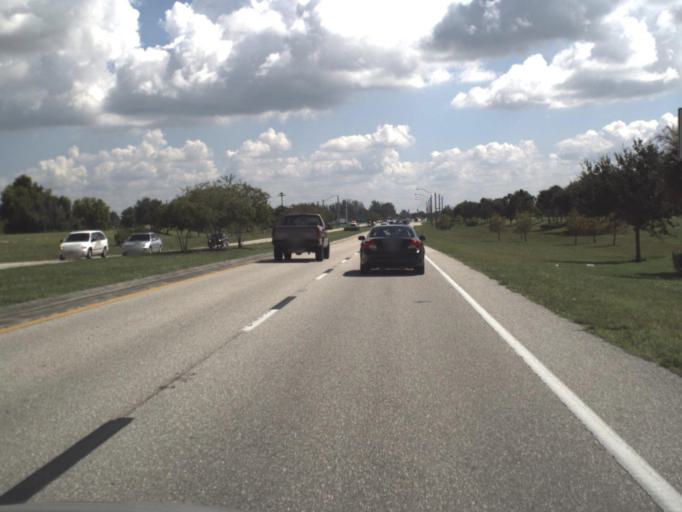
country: US
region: Florida
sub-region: Lee County
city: Cape Coral
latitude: 26.6070
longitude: -81.9961
